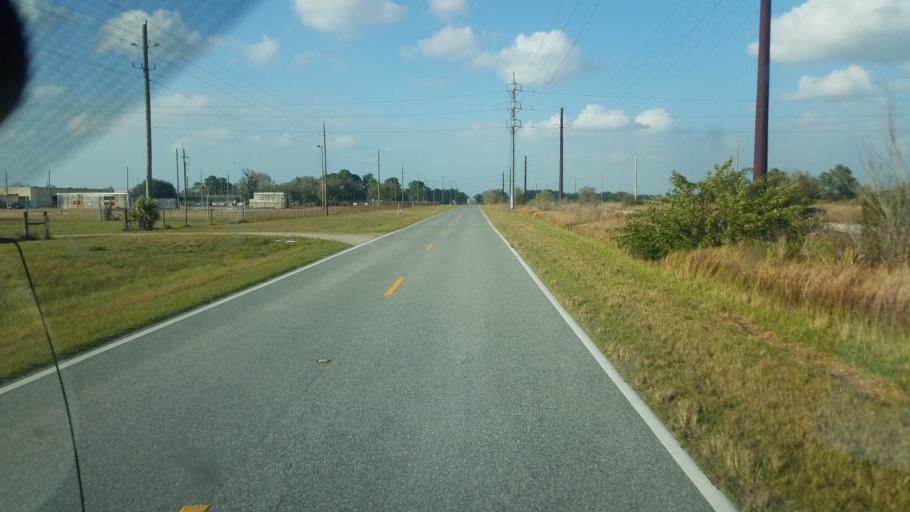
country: US
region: Florida
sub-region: Hardee County
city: Bowling Green
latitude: 27.6279
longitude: -81.9458
